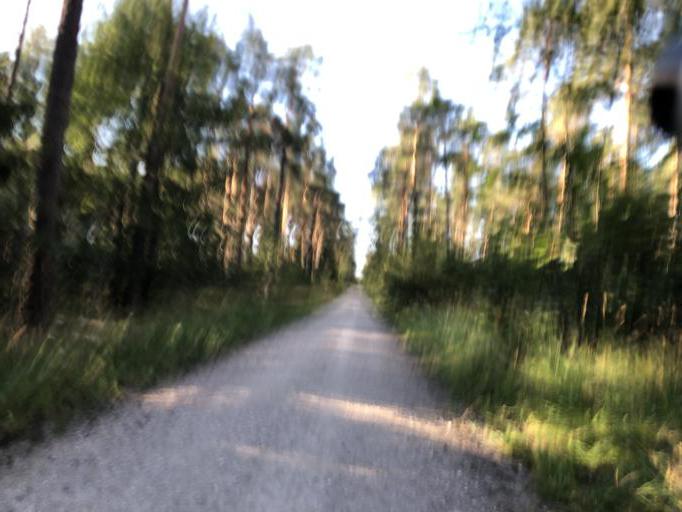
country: DE
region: Bavaria
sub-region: Regierungsbezirk Mittelfranken
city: Kalchreuth
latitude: 49.5547
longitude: 11.0984
